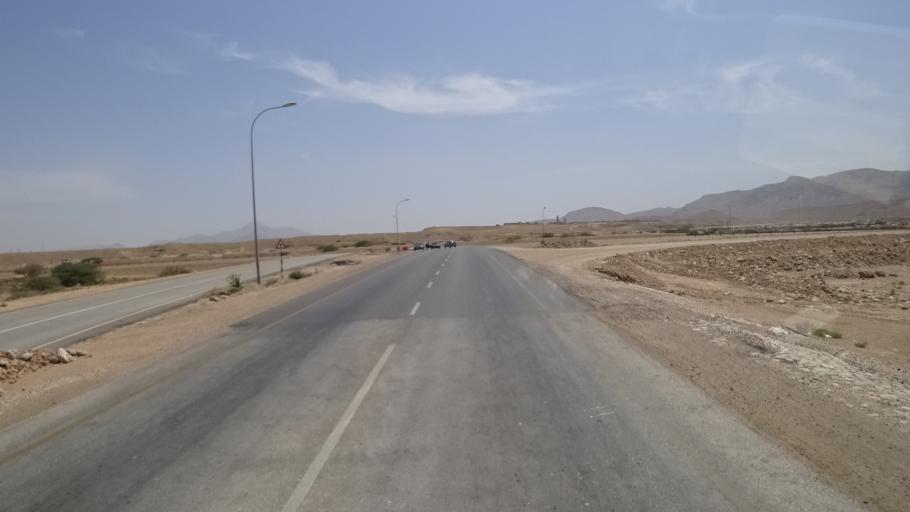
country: OM
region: Ash Sharqiyah
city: Sur
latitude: 22.5799
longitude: 59.4576
